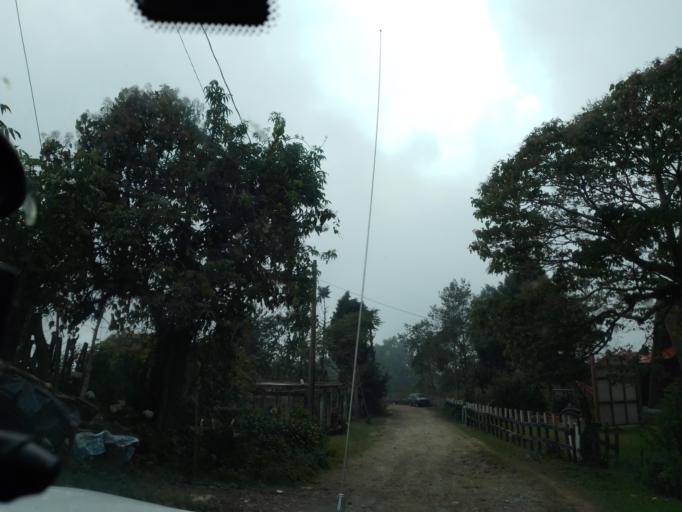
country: MX
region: Chiapas
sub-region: Union Juarez
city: Santo Domingo
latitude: 15.0939
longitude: -92.1004
